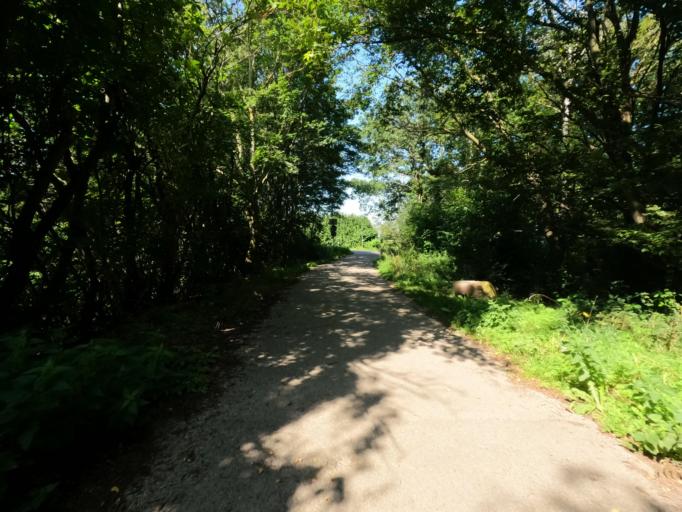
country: DE
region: North Rhine-Westphalia
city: Baesweiler
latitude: 50.9137
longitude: 6.1686
